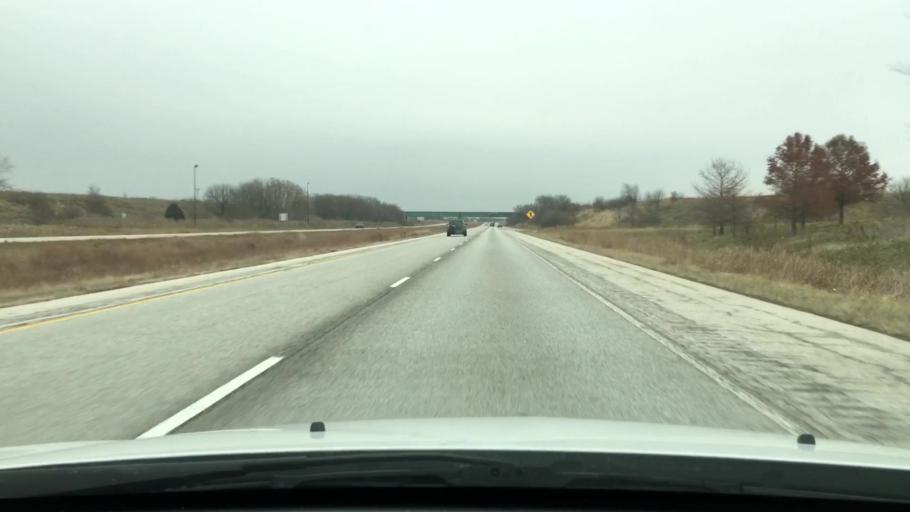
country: US
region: Illinois
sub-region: Morgan County
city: Jacksonville
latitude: 39.7244
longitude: -90.1664
